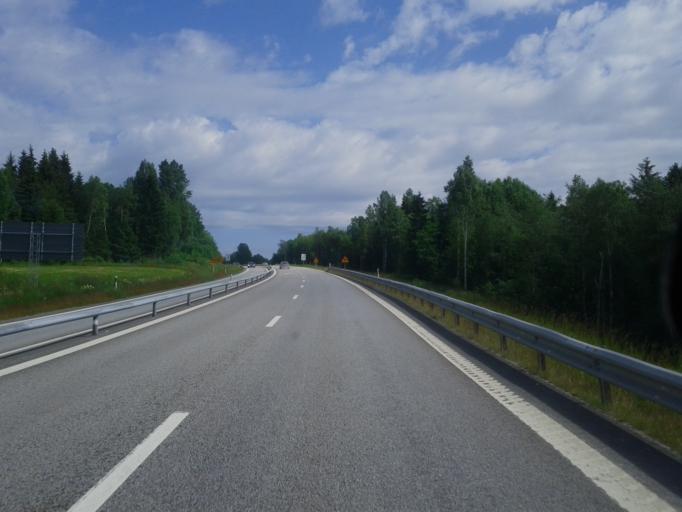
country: SE
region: Vaesternorrland
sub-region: OErnskoeldsviks Kommun
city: Ornskoldsvik
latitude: 63.2977
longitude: 18.8934
